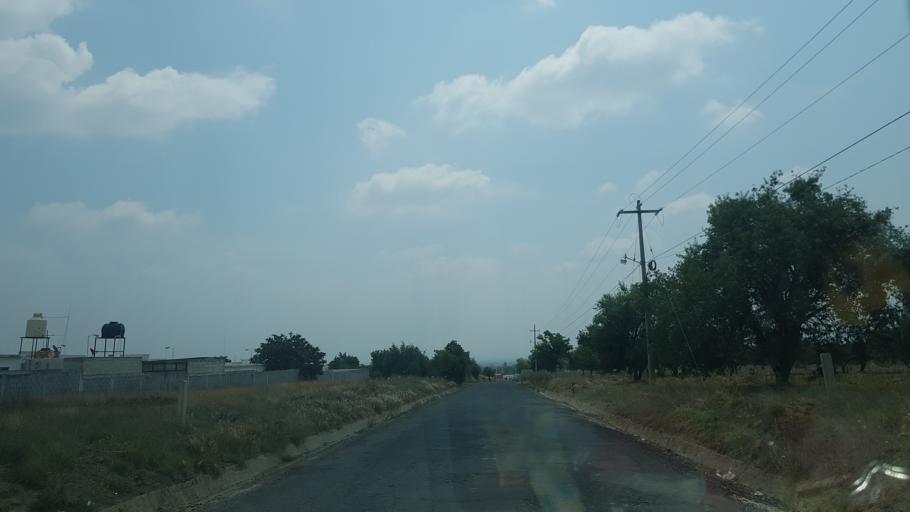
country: MX
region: Puebla
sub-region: Huejotzingo
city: San Juan Pancoac
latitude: 19.1371
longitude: -98.4202
